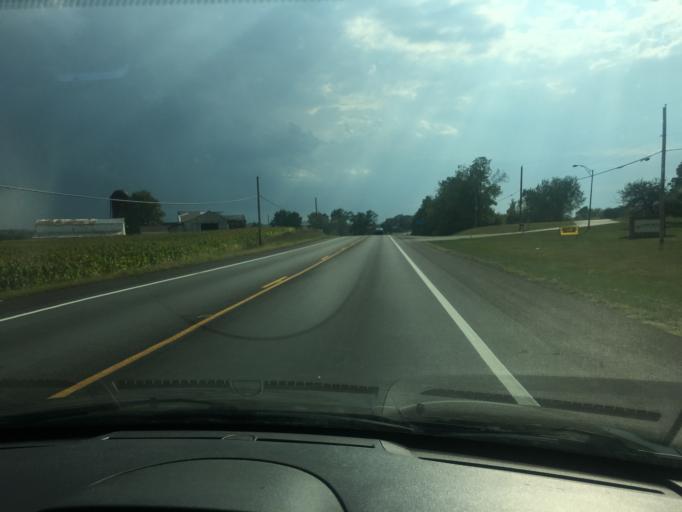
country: US
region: Ohio
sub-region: Champaign County
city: Urbana
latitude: 40.0790
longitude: -83.7634
